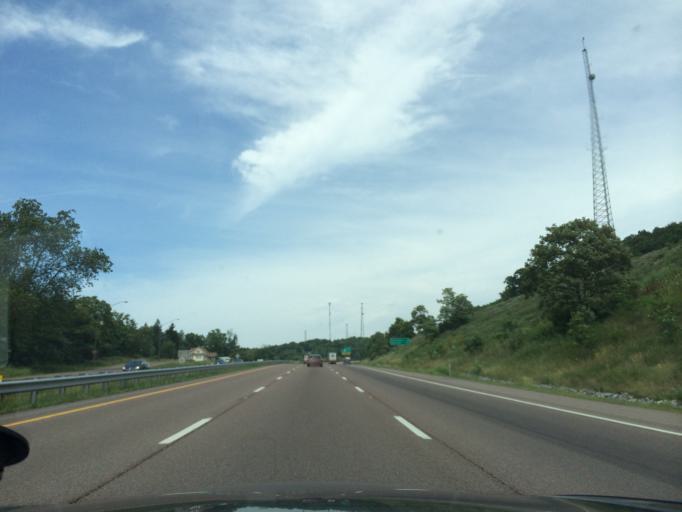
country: US
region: Maryland
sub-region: Allegany County
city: Cumberland
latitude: 39.6996
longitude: -78.6350
